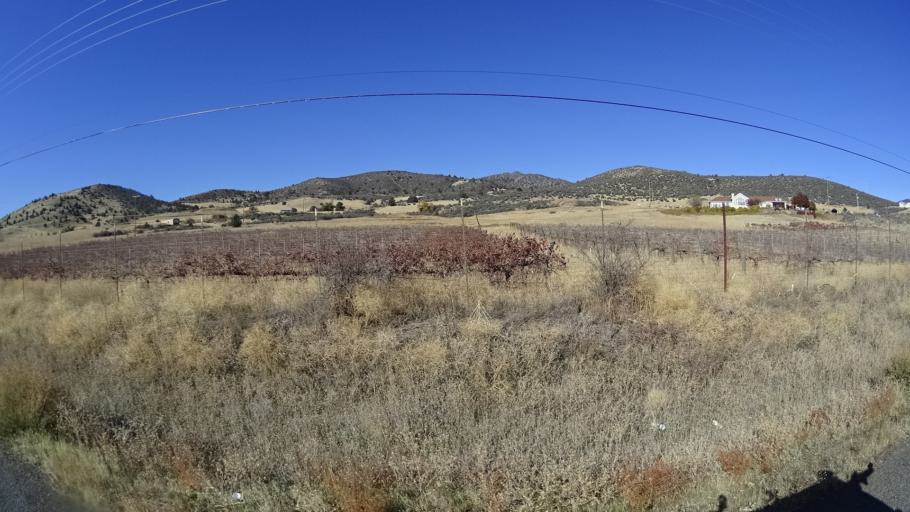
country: US
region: California
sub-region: Siskiyou County
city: Montague
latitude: 41.7962
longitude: -122.5112
